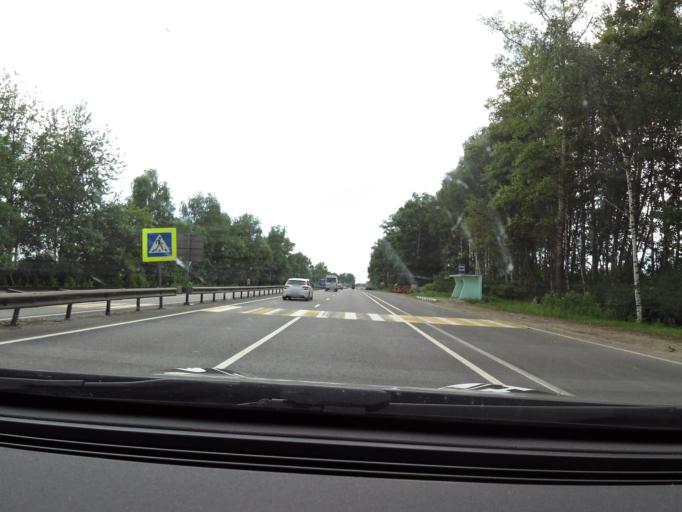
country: RU
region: Vladimir
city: Gorokhovets
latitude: 56.1636
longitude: 42.6130
